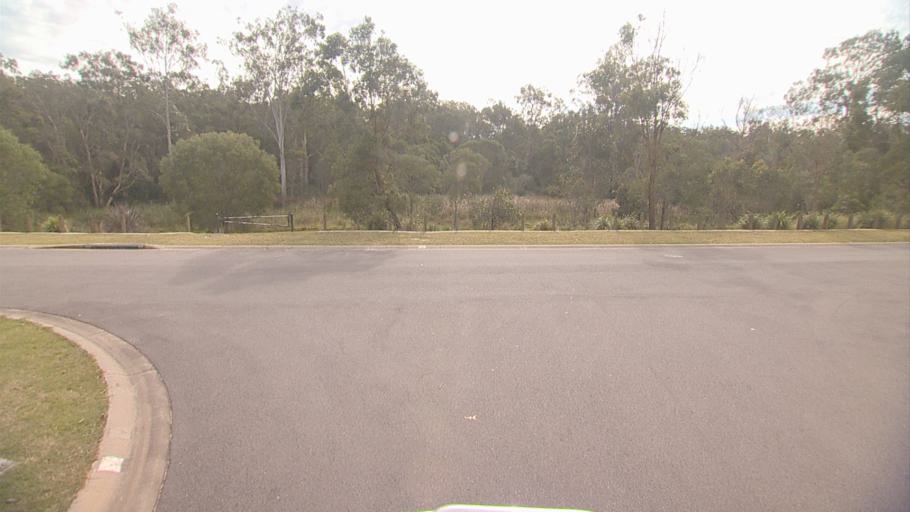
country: AU
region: Queensland
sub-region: Logan
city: Windaroo
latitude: -27.7192
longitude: 153.1683
